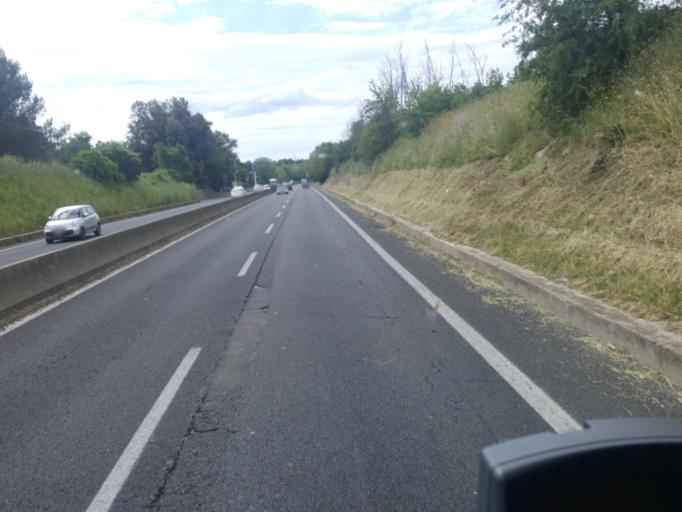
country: IT
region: Latium
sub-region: Citta metropolitana di Roma Capitale
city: La Massimina-Casal Lumbroso
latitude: 41.8873
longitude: 12.3105
